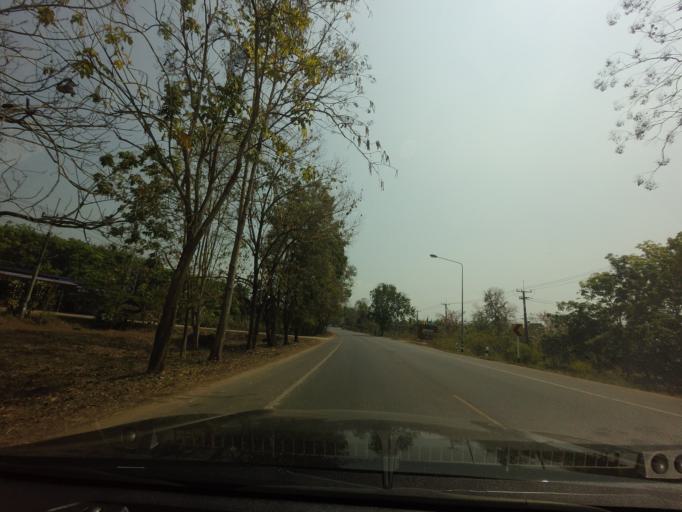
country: TH
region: Kanchanaburi
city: Thong Pha Phum
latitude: 14.6388
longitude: 98.6835
